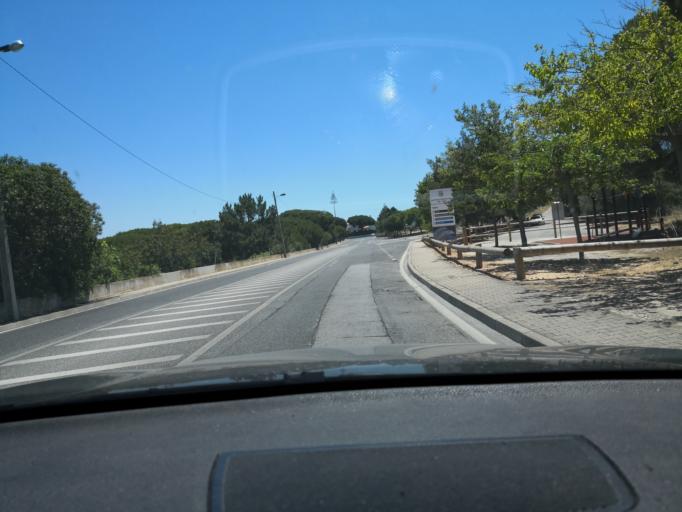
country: PT
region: Faro
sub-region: Albufeira
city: Ferreiras
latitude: 37.1087
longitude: -8.2030
